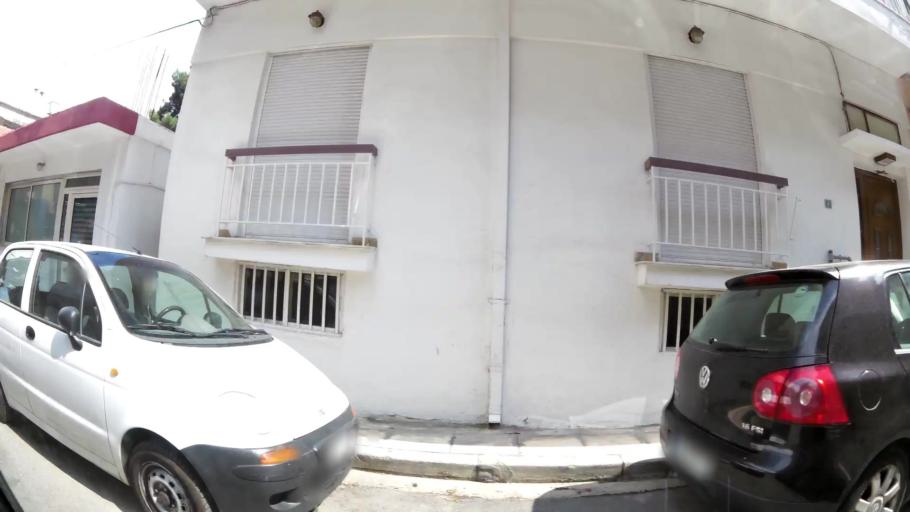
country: GR
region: Central Macedonia
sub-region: Nomos Thessalonikis
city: Polichni
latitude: 40.6640
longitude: 22.9469
